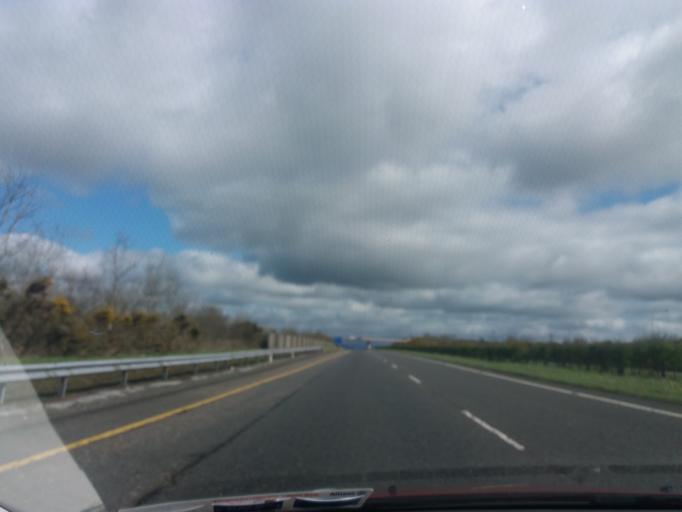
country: IE
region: Munster
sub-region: County Cork
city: Watergrasshill
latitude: 52.0113
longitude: -8.3394
